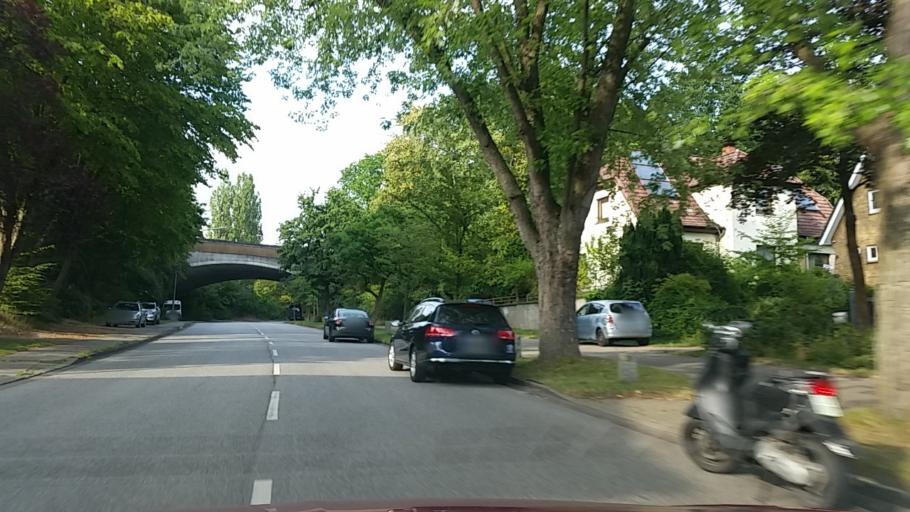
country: DE
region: Hamburg
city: Harburg
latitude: 53.4498
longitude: 9.9708
